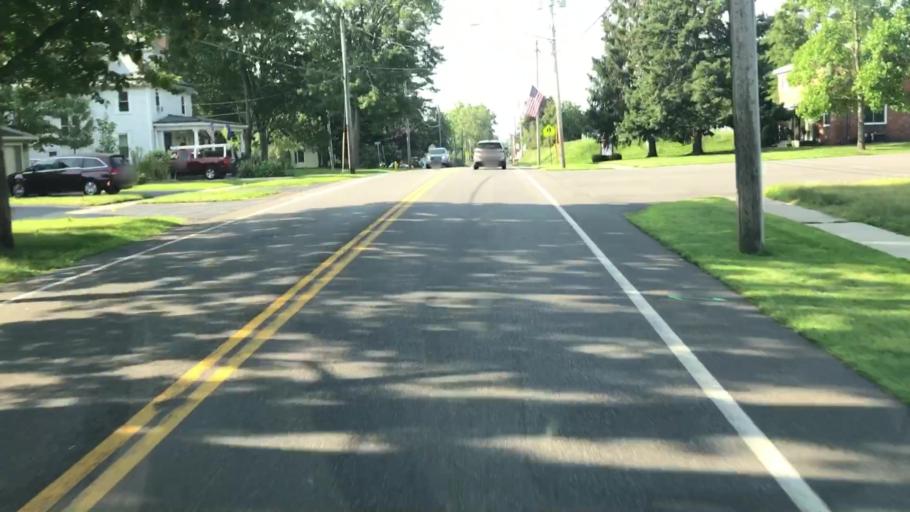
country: US
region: New York
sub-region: Onondaga County
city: Liverpool
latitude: 43.1106
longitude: -76.2059
